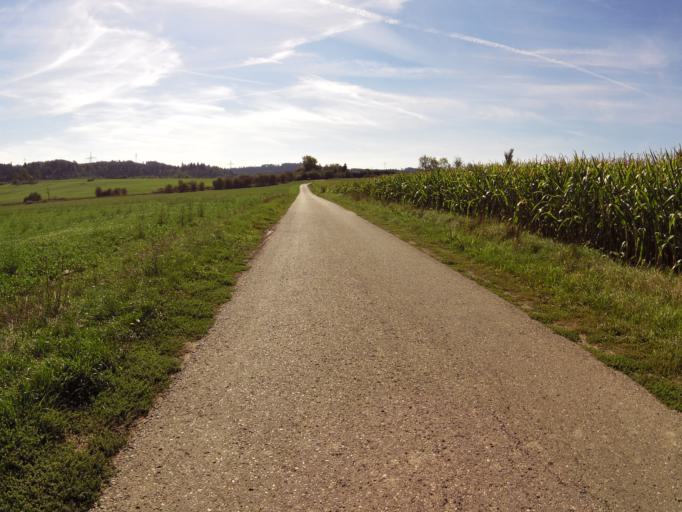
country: DE
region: Baden-Wuerttemberg
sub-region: Freiburg Region
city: Deisslingen
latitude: 48.0949
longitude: 8.5834
